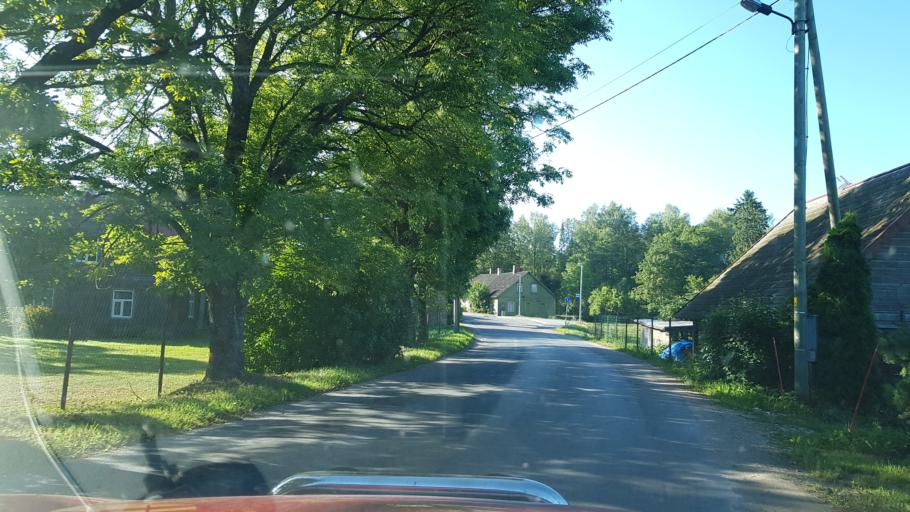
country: EE
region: Jogevamaa
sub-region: Tabivere vald
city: Tabivere
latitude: 58.6867
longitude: 26.5842
